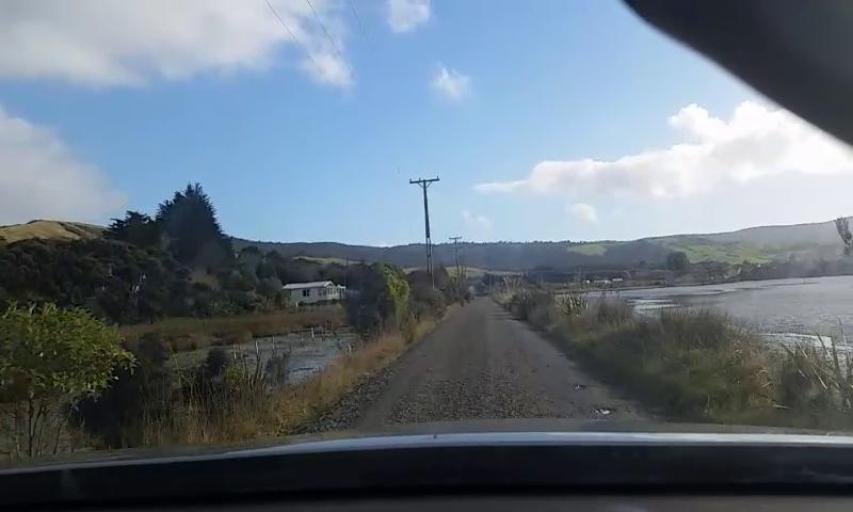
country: NZ
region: Otago
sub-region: Clutha District
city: Papatowai
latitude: -46.6294
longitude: 169.1395
